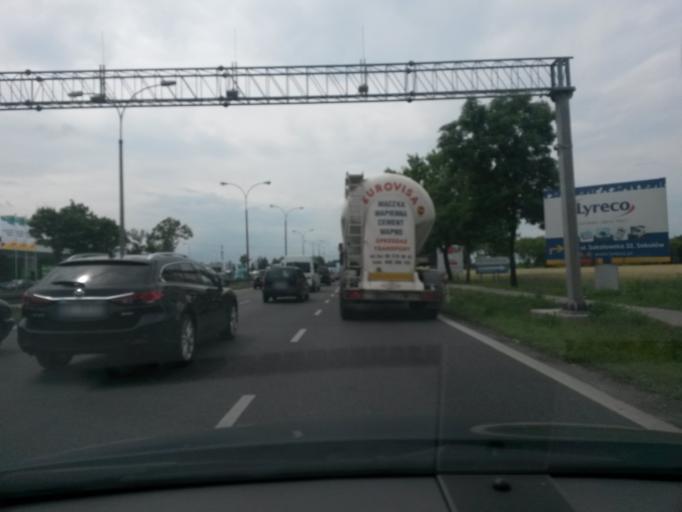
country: PL
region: Masovian Voivodeship
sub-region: Powiat pruszkowski
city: Nowe Grocholice
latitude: 52.1432
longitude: 20.9069
